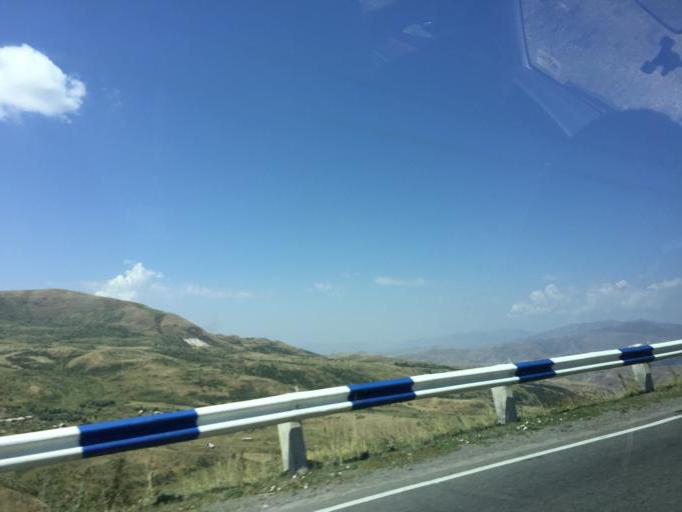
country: AM
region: Vayots' Dzori Marz
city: Jermuk
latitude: 39.6922
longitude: 45.6940
